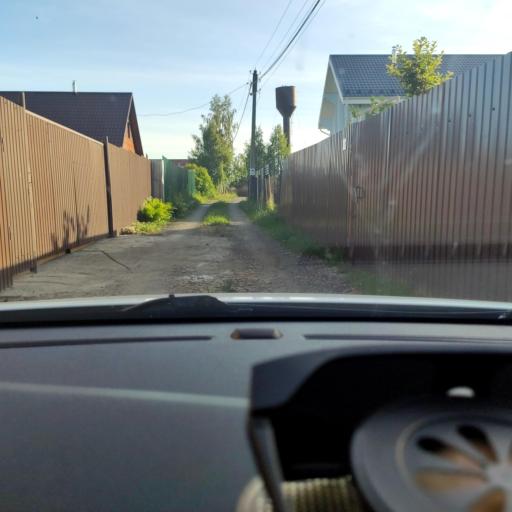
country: RU
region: Tatarstan
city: Stolbishchi
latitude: 55.6943
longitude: 49.1912
